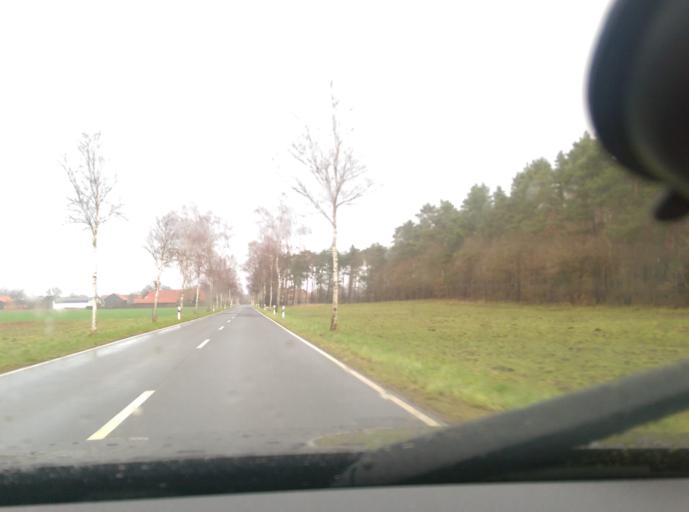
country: DE
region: Lower Saxony
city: Schwarmstedt
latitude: 52.6524
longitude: 9.6140
